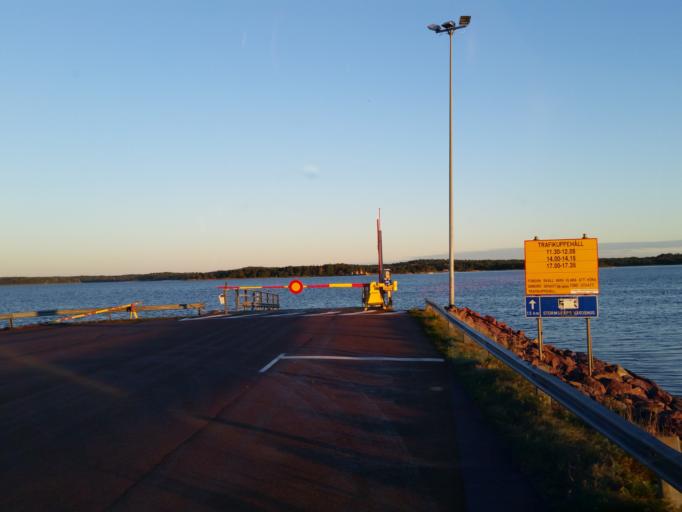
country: AX
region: Alands skaergard
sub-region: Vardoe
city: Vardoe
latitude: 60.3219
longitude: 20.3728
